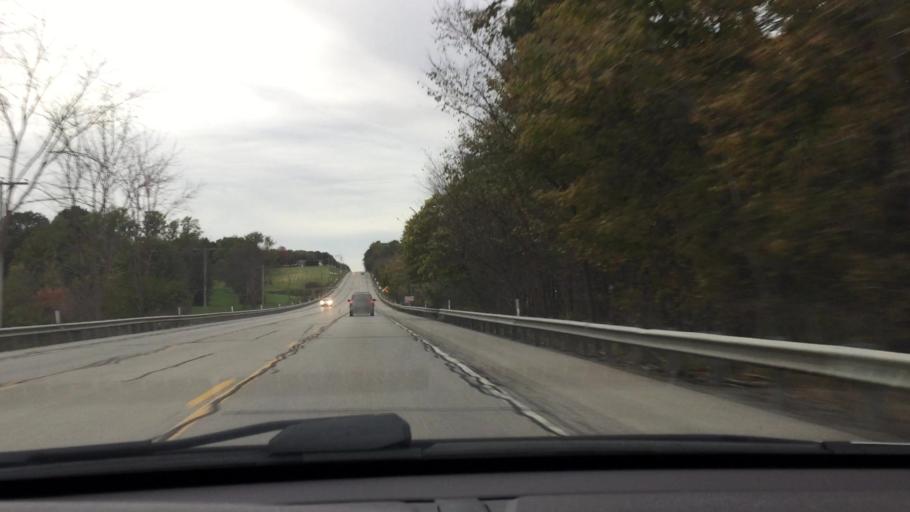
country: US
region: Ohio
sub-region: Mahoning County
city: Lowellville
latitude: 41.0770
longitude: -80.4830
